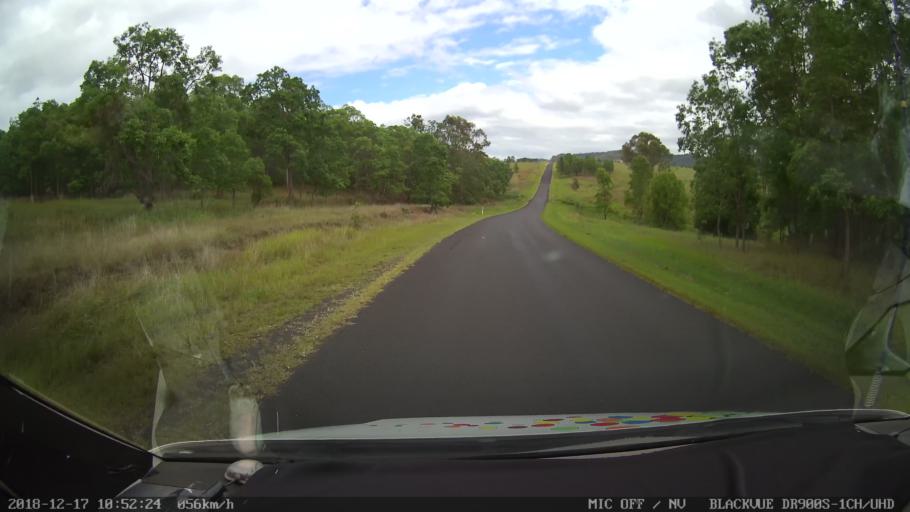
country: AU
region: New South Wales
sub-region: Tenterfield Municipality
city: Carrolls Creek
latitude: -28.8457
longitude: 152.5637
